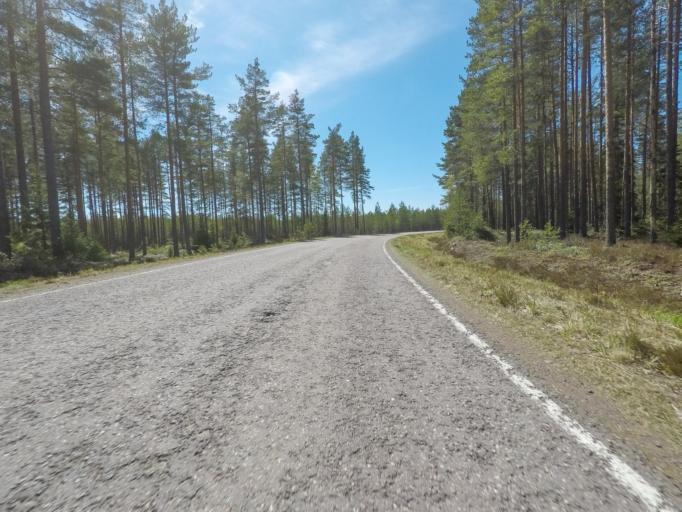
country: FI
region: Uusimaa
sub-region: Helsinki
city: Kaerkoelae
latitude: 60.6074
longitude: 23.8323
